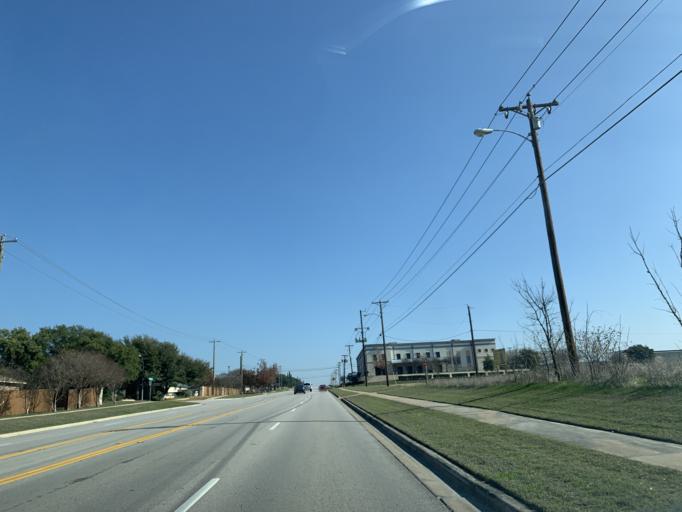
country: US
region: Texas
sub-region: Travis County
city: Windemere
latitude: 30.4965
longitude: -97.6314
